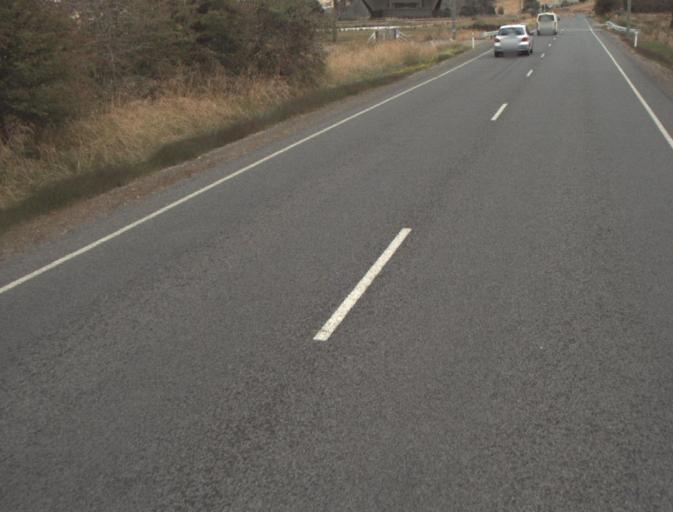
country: AU
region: Tasmania
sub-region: Launceston
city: Mayfield
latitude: -41.2429
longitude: 147.2166
